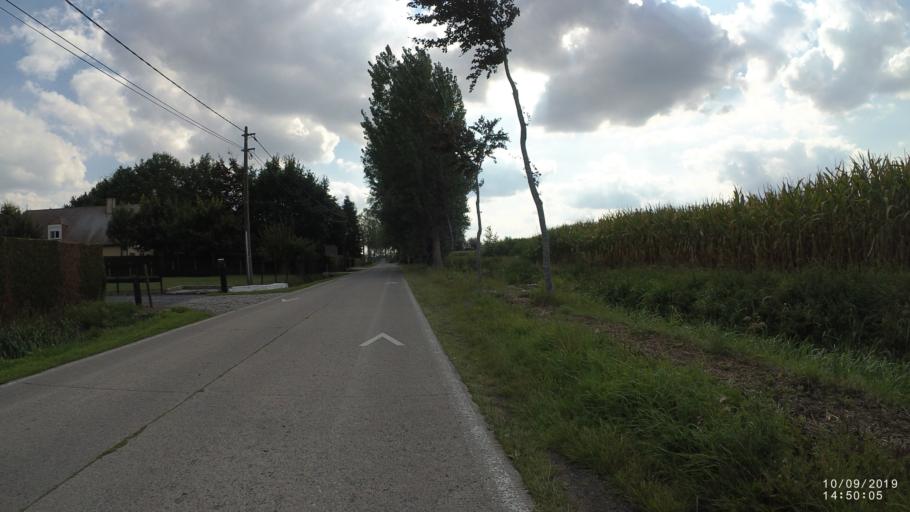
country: BE
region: Flanders
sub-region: Provincie Oost-Vlaanderen
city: Evergem
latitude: 51.1584
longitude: 3.6945
